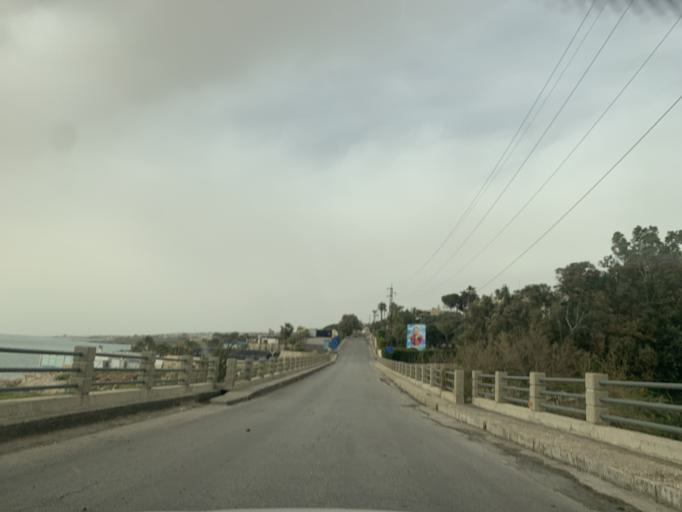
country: LB
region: Mont-Liban
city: Jbail
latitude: 34.1017
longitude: 35.6516
